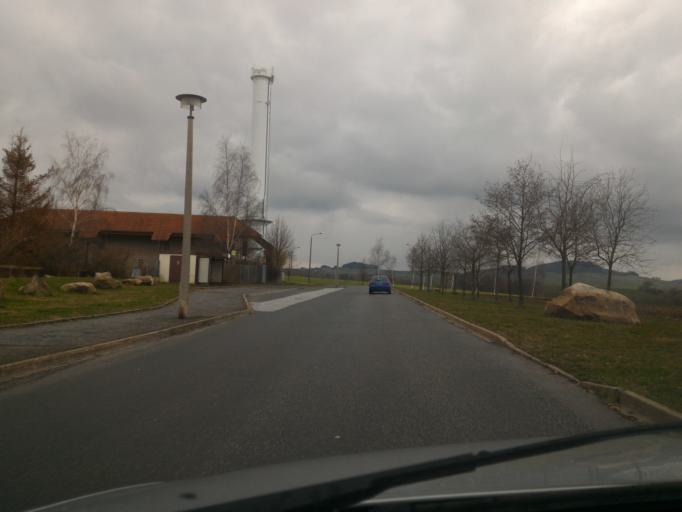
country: DE
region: Saxony
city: Olbersdorf
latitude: 50.8744
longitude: 14.7581
